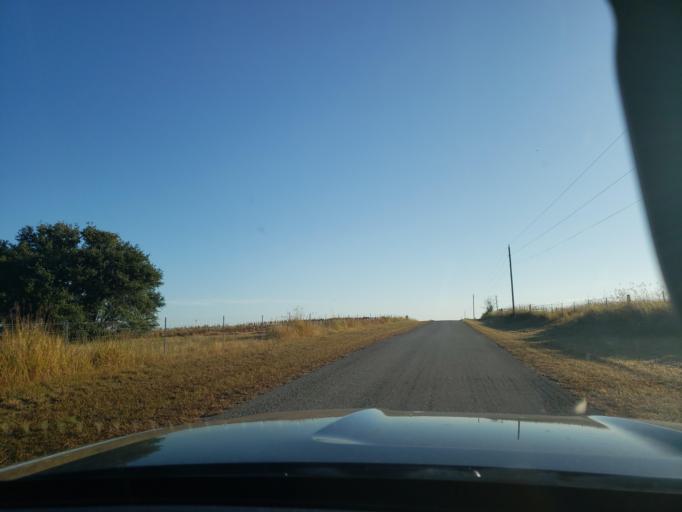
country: US
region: Texas
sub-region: Bee County
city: Beeville
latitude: 28.4255
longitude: -97.7013
